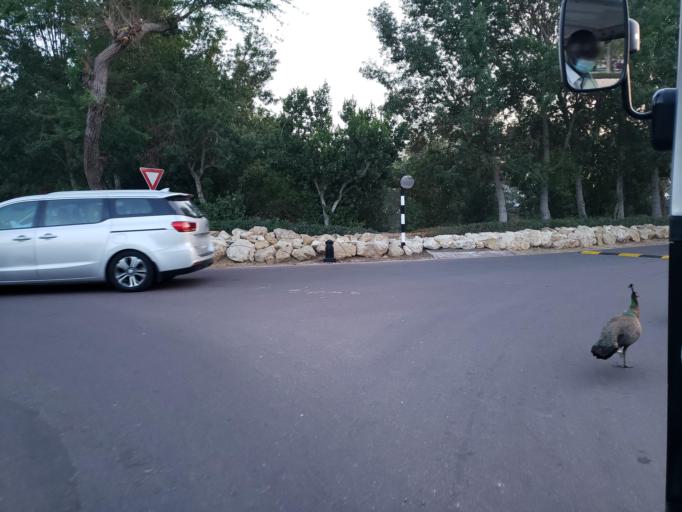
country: AE
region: Dubai
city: Dubai
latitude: 24.9862
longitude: 55.0225
